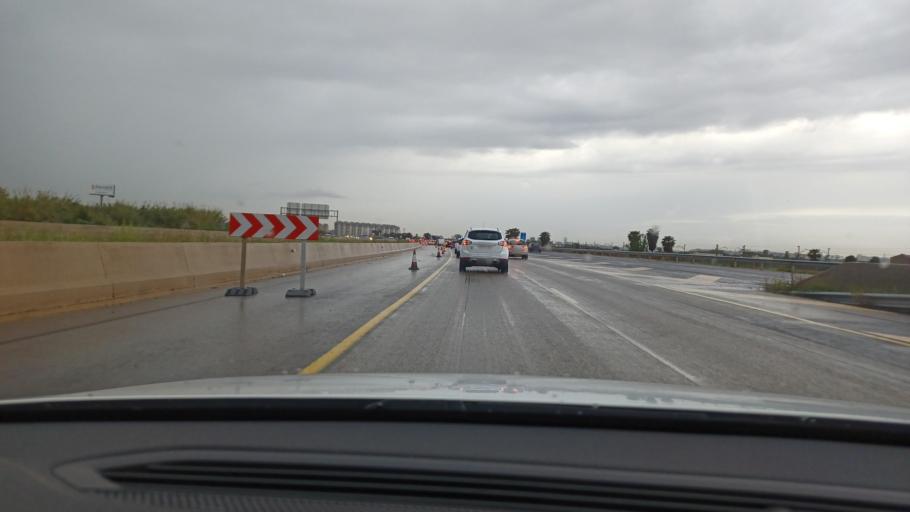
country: ES
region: Valencia
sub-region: Provincia de Valencia
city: Alboraya
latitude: 39.5083
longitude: -0.3255
